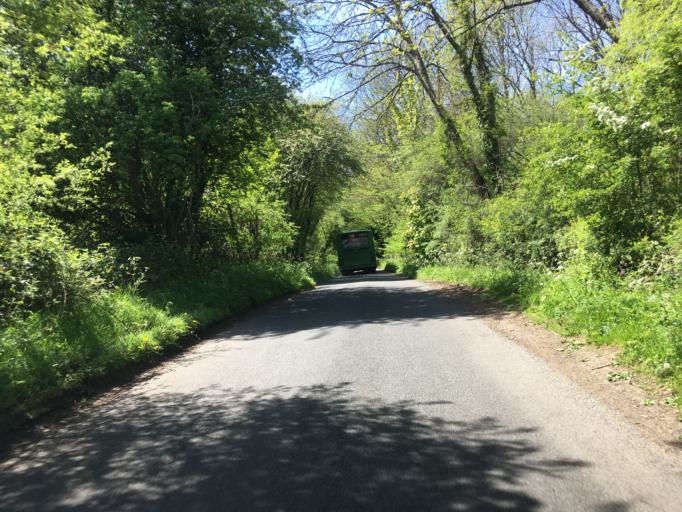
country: GB
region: England
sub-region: Gloucestershire
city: Coates
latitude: 51.7259
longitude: -2.0879
